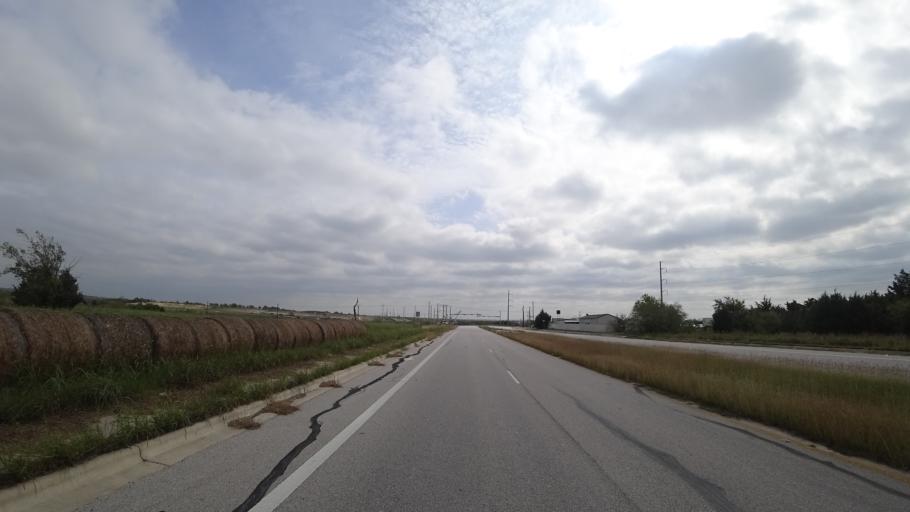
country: US
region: Texas
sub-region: Travis County
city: Pflugerville
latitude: 30.3790
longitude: -97.6101
